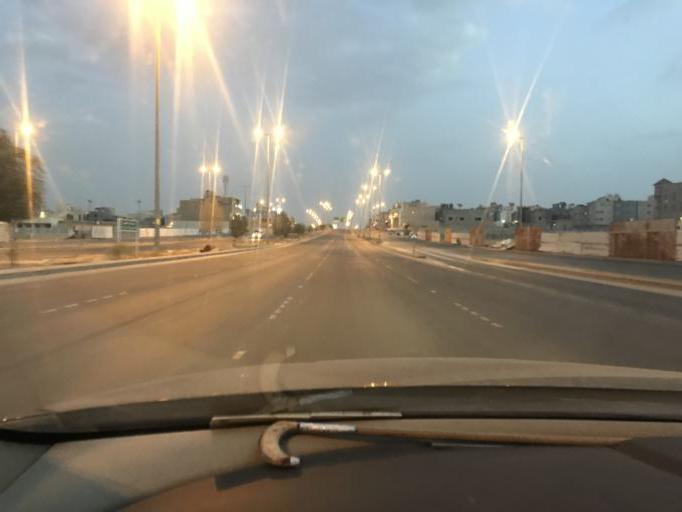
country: SA
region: Ar Riyad
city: Riyadh
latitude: 24.8435
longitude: 46.6748
